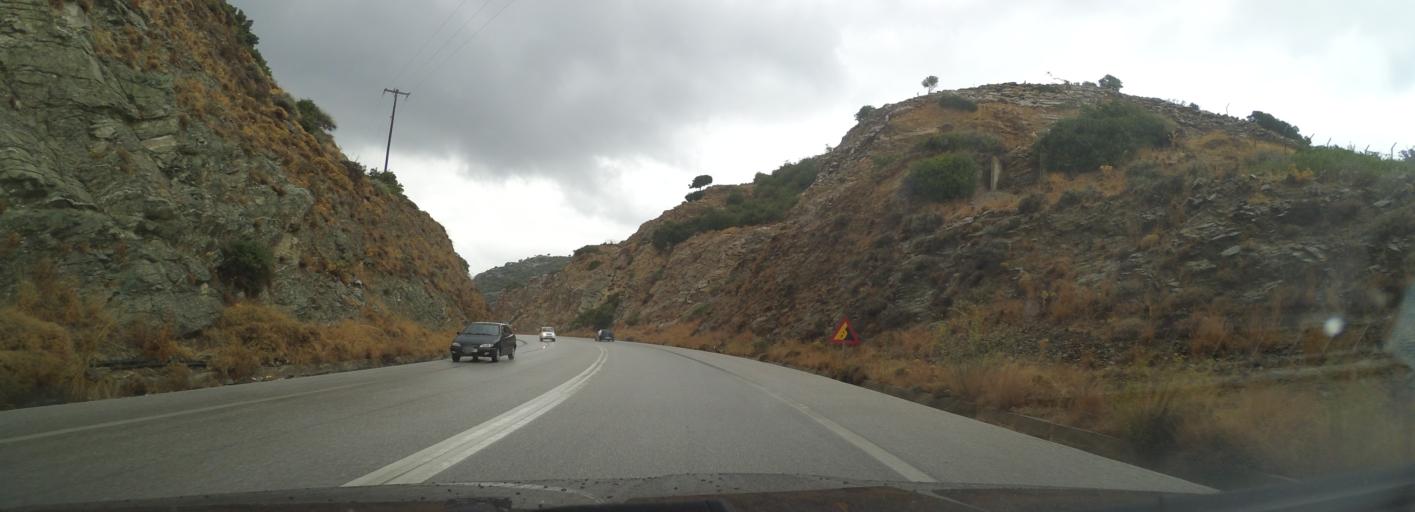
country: GR
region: Crete
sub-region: Nomos Irakleiou
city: Tilisos
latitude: 35.4066
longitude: 24.9862
